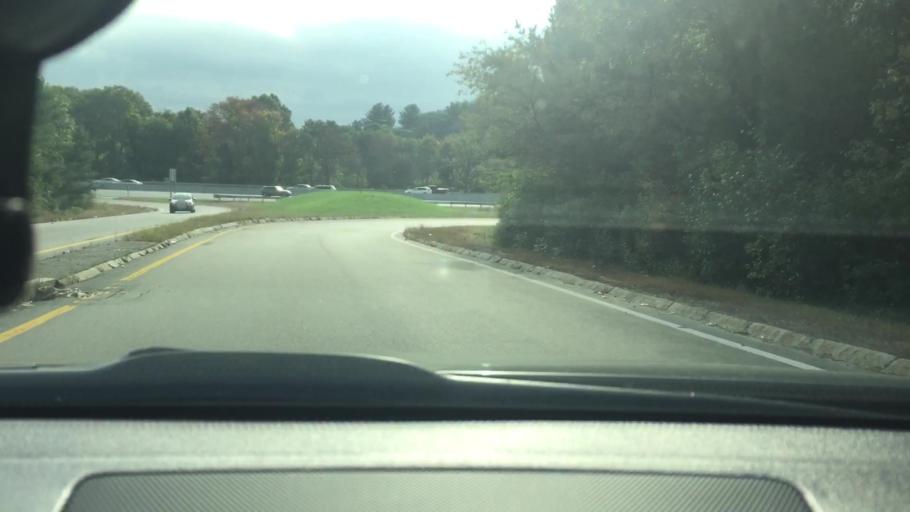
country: US
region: Massachusetts
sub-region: Norfolk County
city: Needham
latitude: 42.2691
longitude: -71.2030
